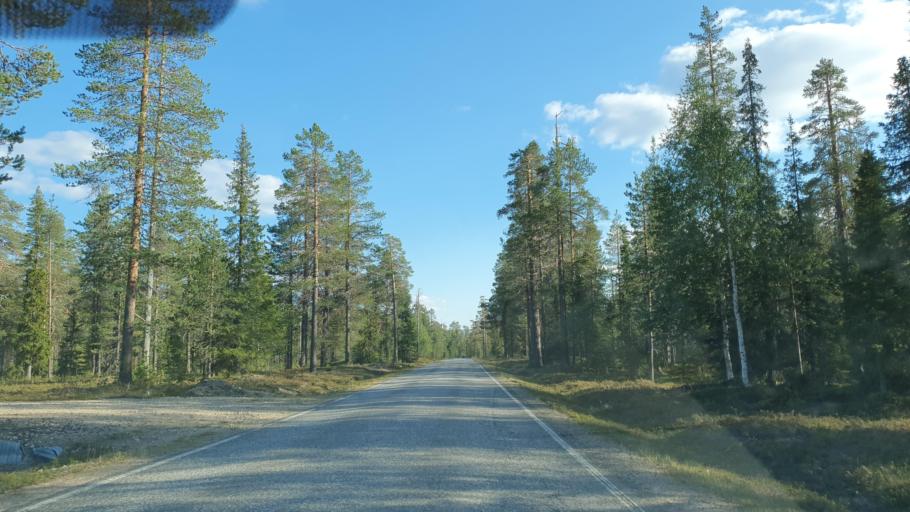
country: FI
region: Lapland
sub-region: Tunturi-Lappi
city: Kolari
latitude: 67.6629
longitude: 24.1634
